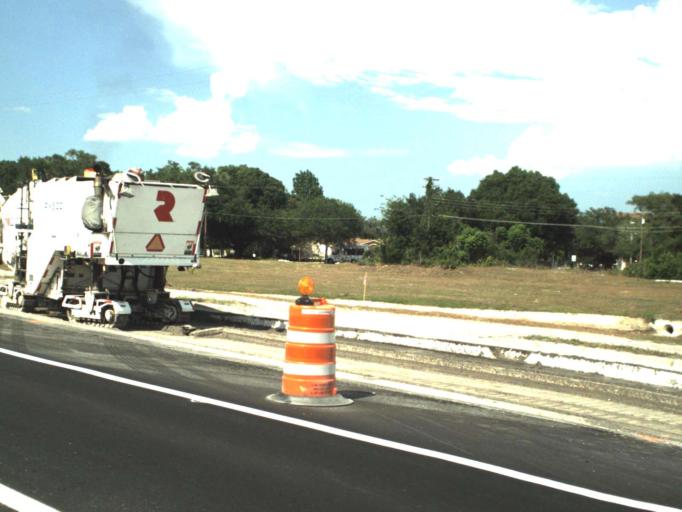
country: US
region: Florida
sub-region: Seminole County
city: Casselberry
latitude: 28.6642
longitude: -81.3403
